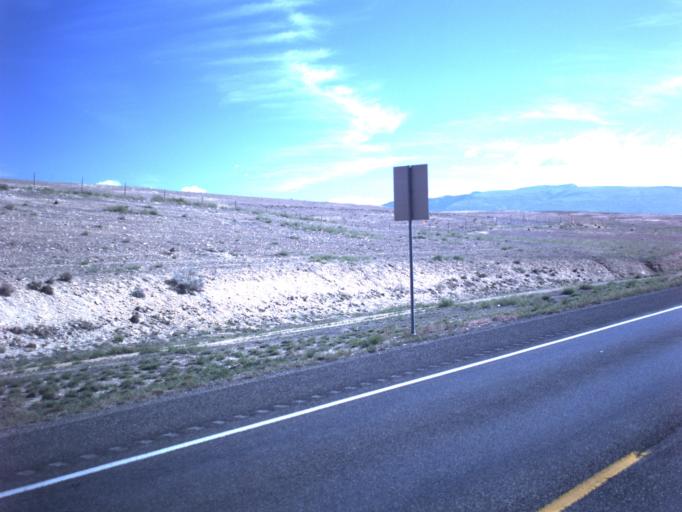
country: US
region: Utah
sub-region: Sanpete County
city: Gunnison
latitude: 39.1711
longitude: -111.8294
